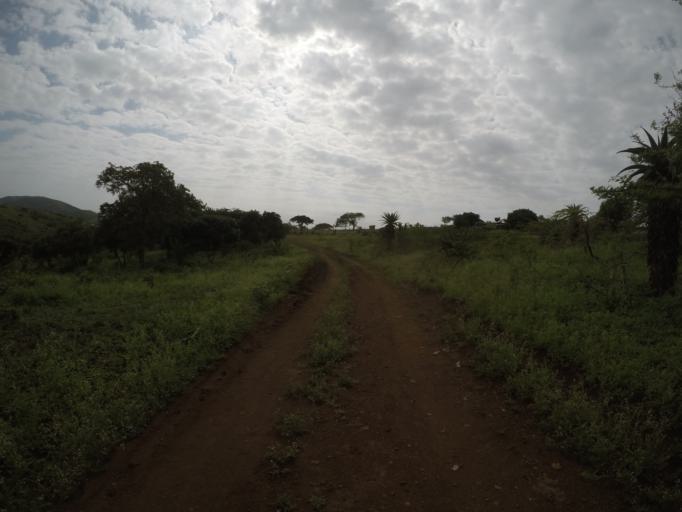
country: ZA
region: KwaZulu-Natal
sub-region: uThungulu District Municipality
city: Empangeni
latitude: -28.6281
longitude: 31.9071
